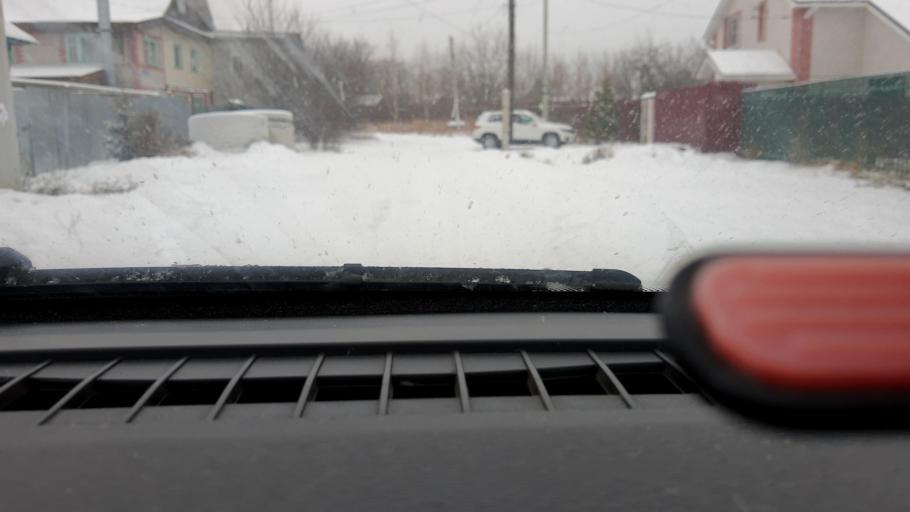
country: RU
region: Nizjnij Novgorod
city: Novaya Balakhna
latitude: 56.5173
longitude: 43.5728
